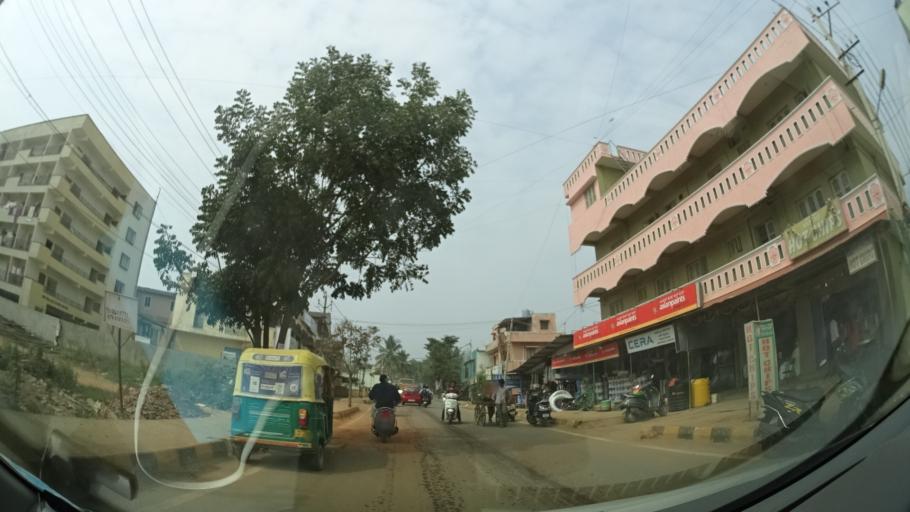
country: IN
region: Karnataka
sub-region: Bangalore Rural
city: Hoskote
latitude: 12.9676
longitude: 77.7584
